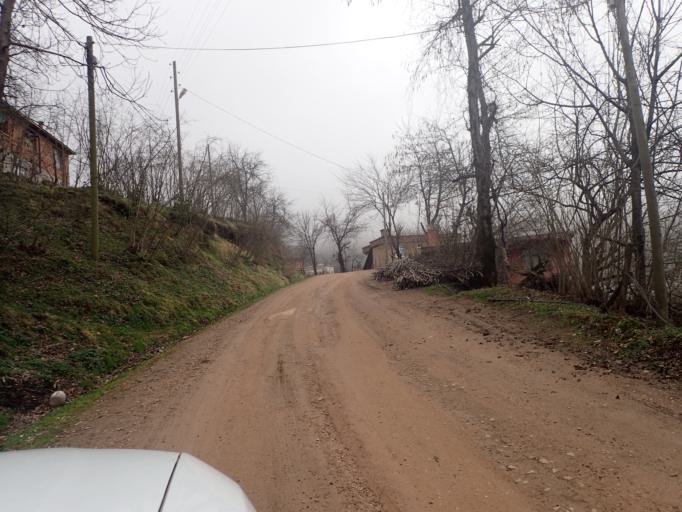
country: TR
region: Ordu
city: Camas
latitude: 40.9103
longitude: 37.5656
